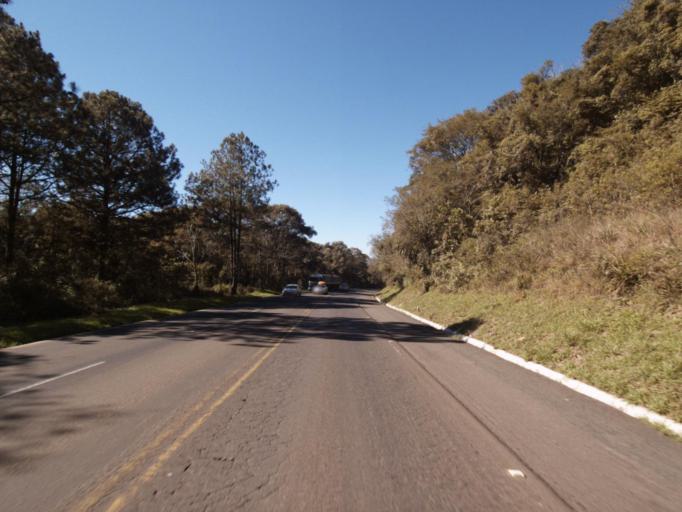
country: BR
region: Santa Catarina
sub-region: Sao Lourenco Do Oeste
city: Sao Lourenco dOeste
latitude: -26.8200
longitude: -53.1557
